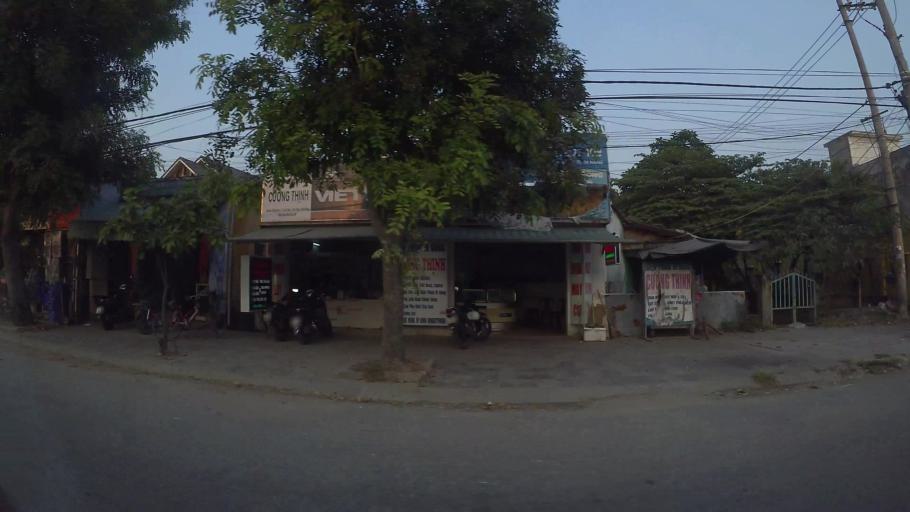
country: VN
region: Quang Nam
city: Quang Nam
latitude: 15.9479
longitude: 108.2202
